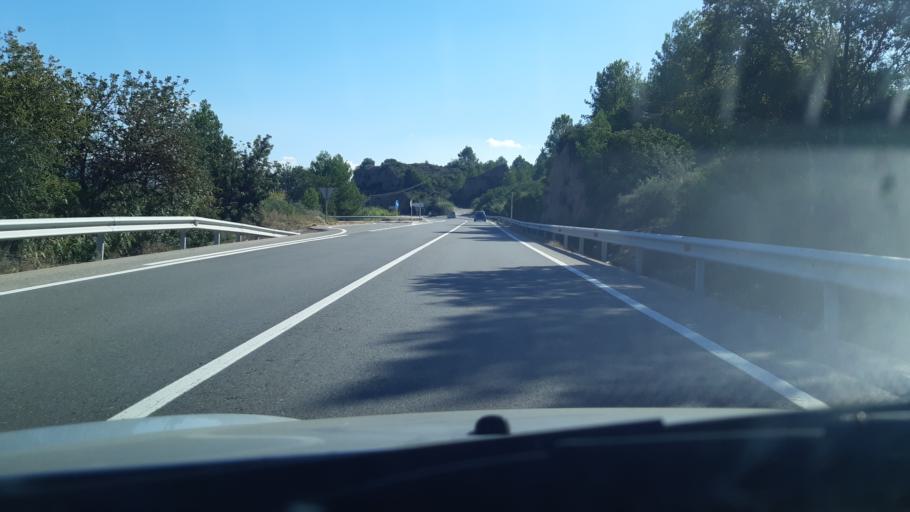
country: ES
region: Catalonia
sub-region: Provincia de Tarragona
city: Tivenys
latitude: 40.8997
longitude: 0.4842
